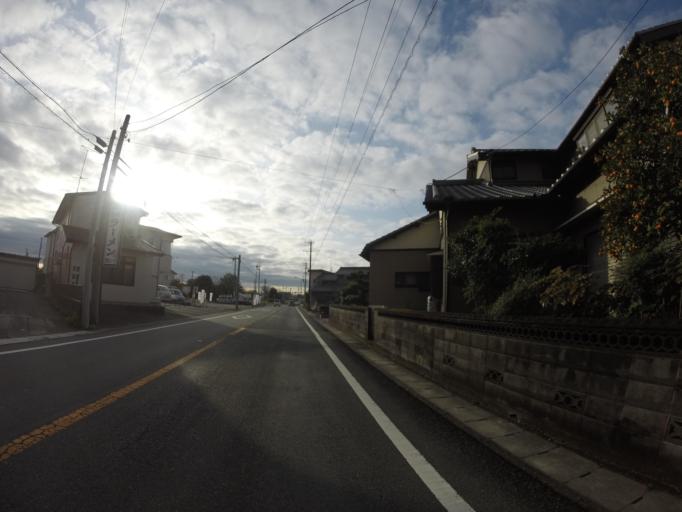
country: JP
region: Shizuoka
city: Hamakita
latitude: 34.8151
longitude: 137.7781
